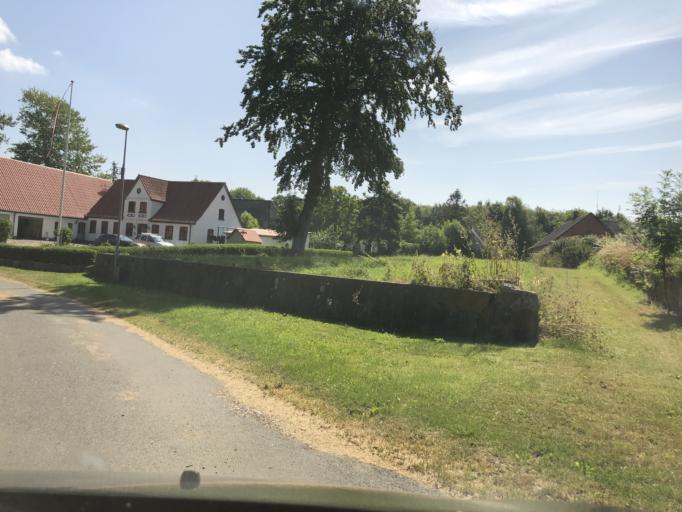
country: DK
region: South Denmark
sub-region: Faaborg-Midtfyn Kommune
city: Faaborg
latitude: 54.9570
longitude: 10.2242
